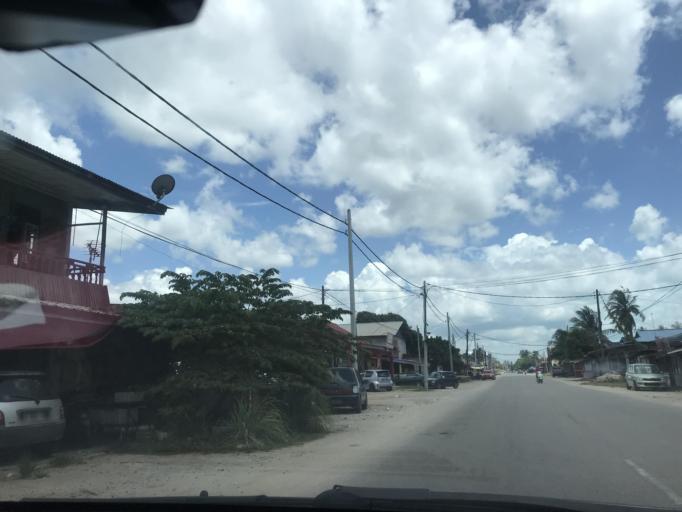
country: TH
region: Narathiwat
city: Tak Bai
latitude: 6.2252
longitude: 102.1041
